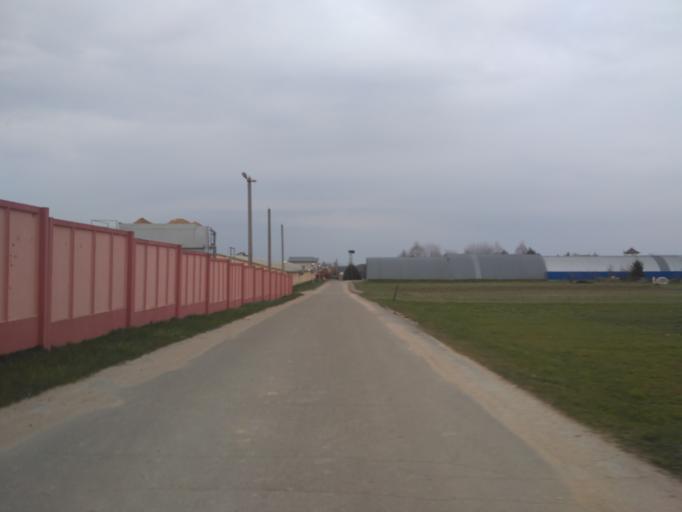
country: BY
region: Minsk
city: Slabada
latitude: 54.0035
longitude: 27.8785
